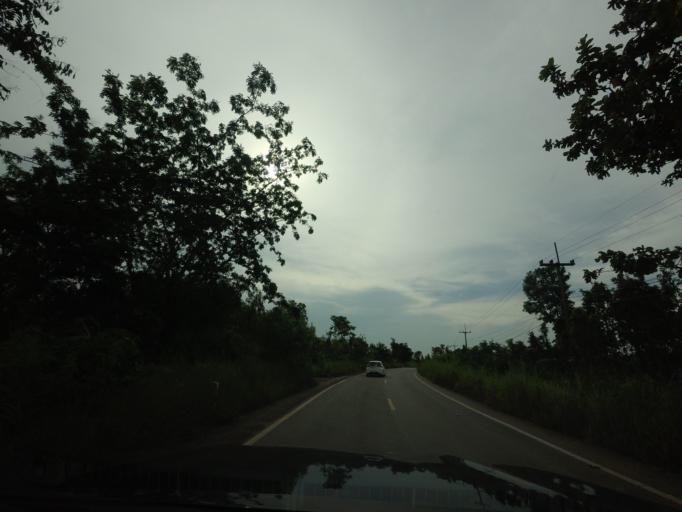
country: TH
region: Changwat Nong Bua Lamphu
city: Na Klang
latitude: 17.3701
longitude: 102.3554
